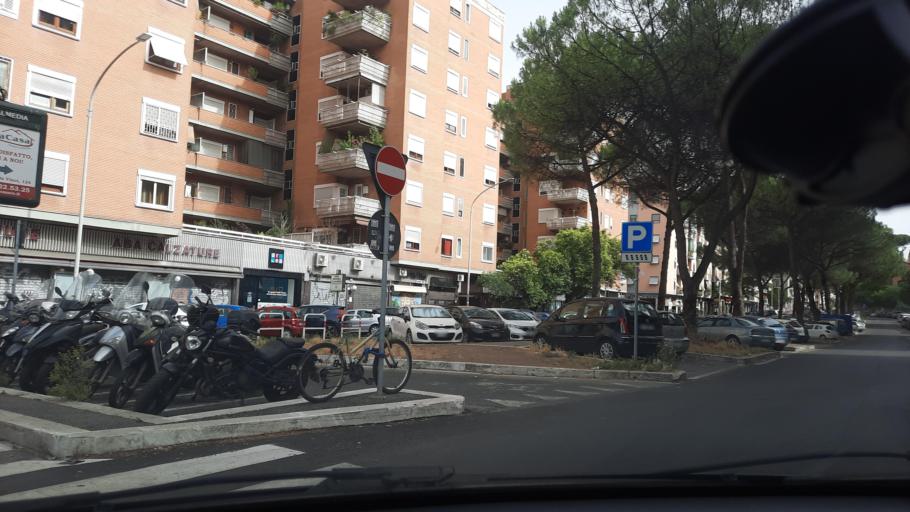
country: IT
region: Latium
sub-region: Citta metropolitana di Roma Capitale
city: Rome
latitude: 41.8564
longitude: 12.4806
